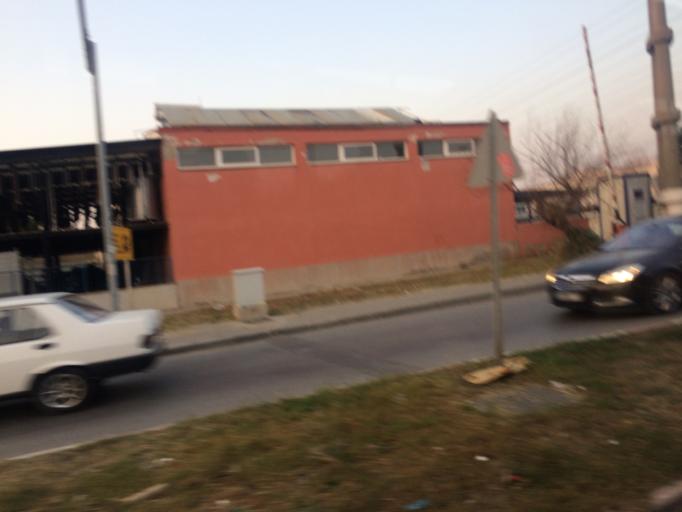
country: TR
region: Izmir
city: Karsiyaka
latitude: 38.4984
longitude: 27.0444
